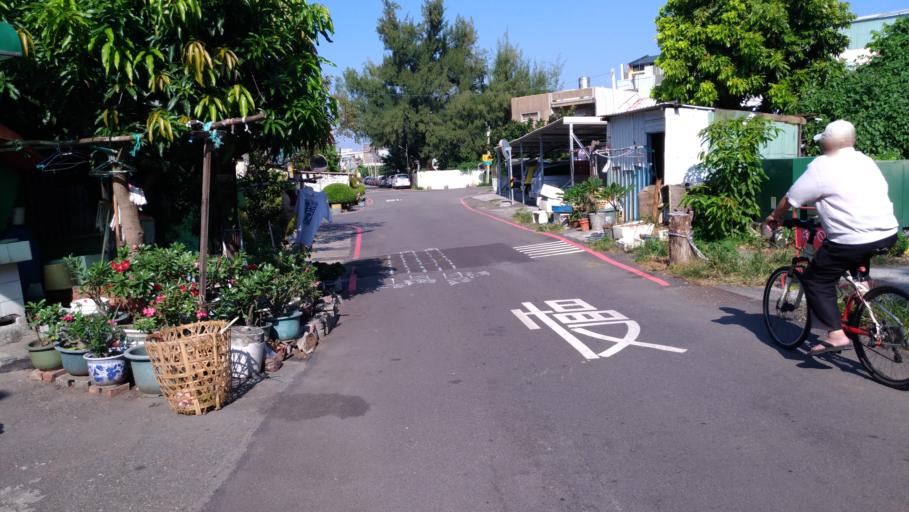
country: TW
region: Taiwan
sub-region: Changhua
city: Chang-hua
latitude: 24.0876
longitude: 120.5404
